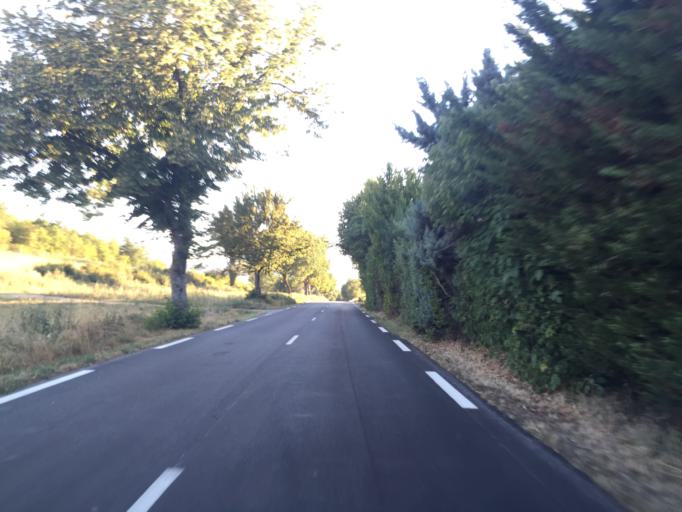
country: FR
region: Provence-Alpes-Cote d'Azur
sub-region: Departement des Alpes-de-Haute-Provence
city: Reillanne
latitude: 43.8838
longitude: 5.7142
